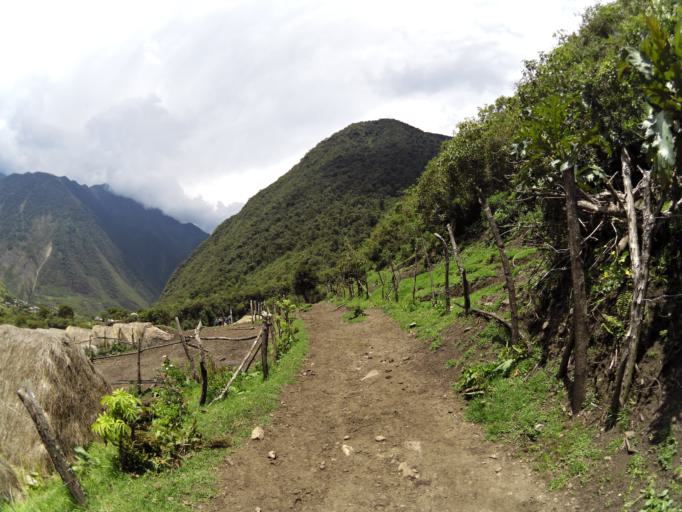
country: PE
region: Cusco
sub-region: Provincia de La Convencion
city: Santa Teresa
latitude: -13.3243
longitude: -72.6644
